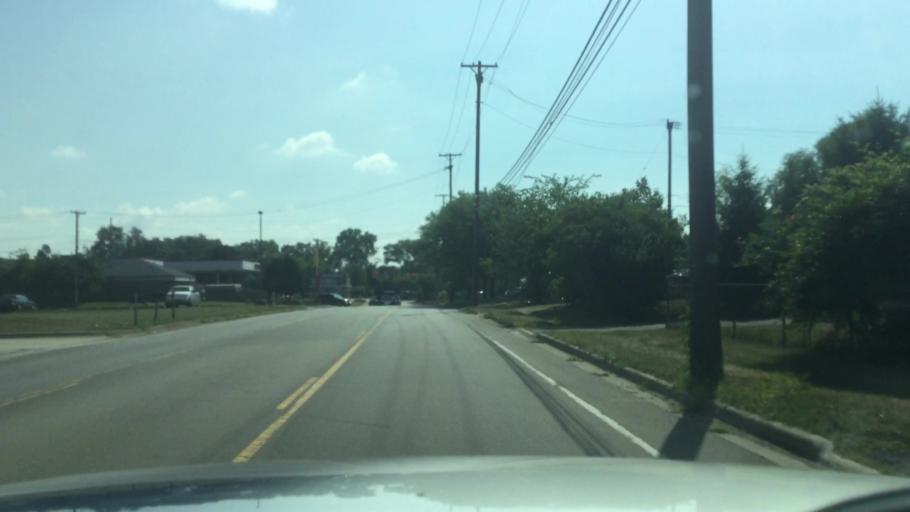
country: US
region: Michigan
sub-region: Wayne County
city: Belleville
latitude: 42.2137
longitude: -83.5458
